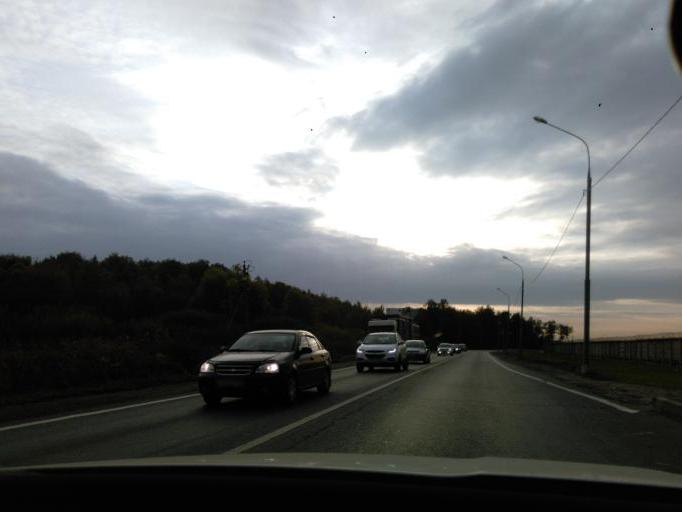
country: RU
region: Moskovskaya
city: Lobnya
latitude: 55.9829
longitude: 37.4465
